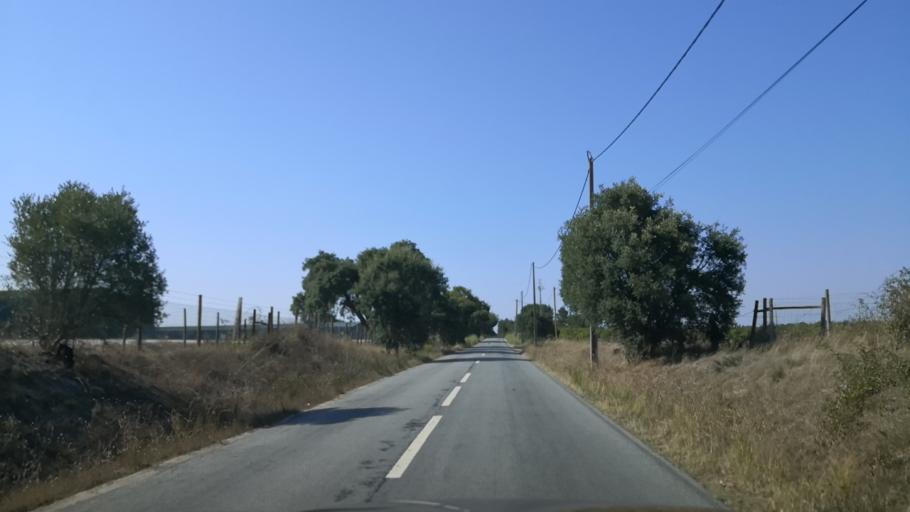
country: PT
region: Evora
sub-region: Vendas Novas
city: Vendas Novas
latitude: 38.7189
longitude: -8.6187
